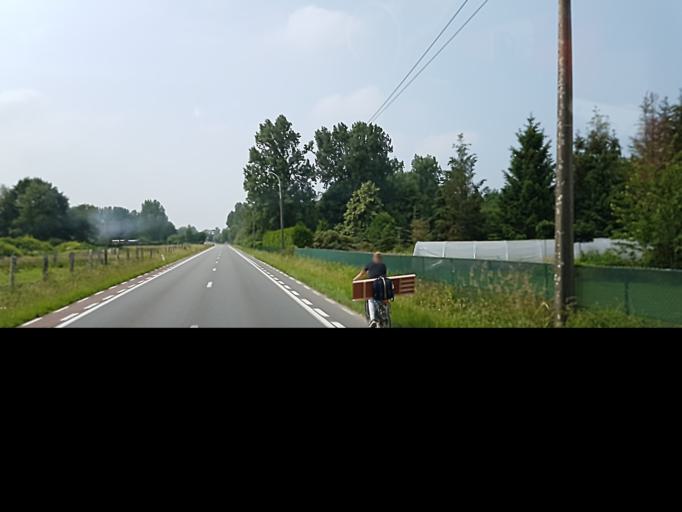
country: BE
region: Flanders
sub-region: Provincie Antwerpen
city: Nijlen
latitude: 51.1714
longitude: 4.6427
